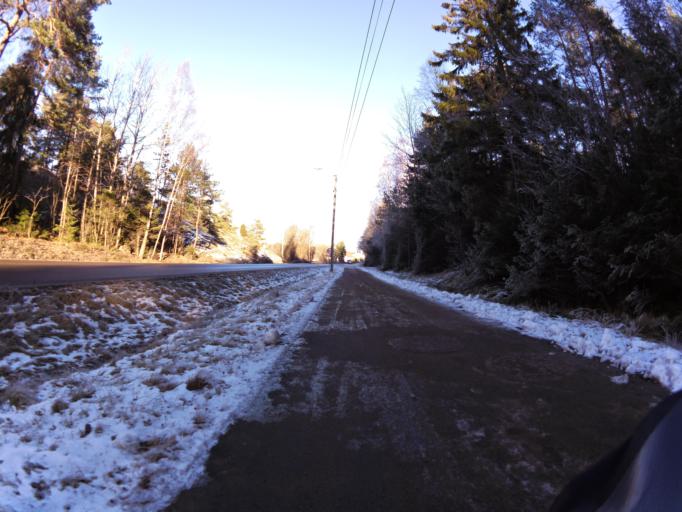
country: NO
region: Ostfold
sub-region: Fredrikstad
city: Fredrikstad
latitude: 59.2007
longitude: 10.8711
